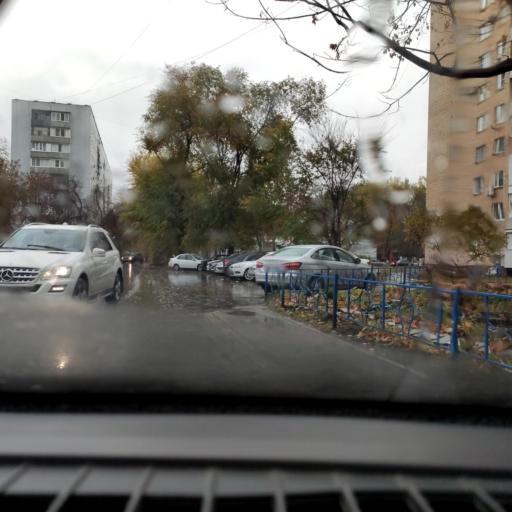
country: RU
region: Samara
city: Tol'yatti
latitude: 53.5322
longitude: 49.2755
